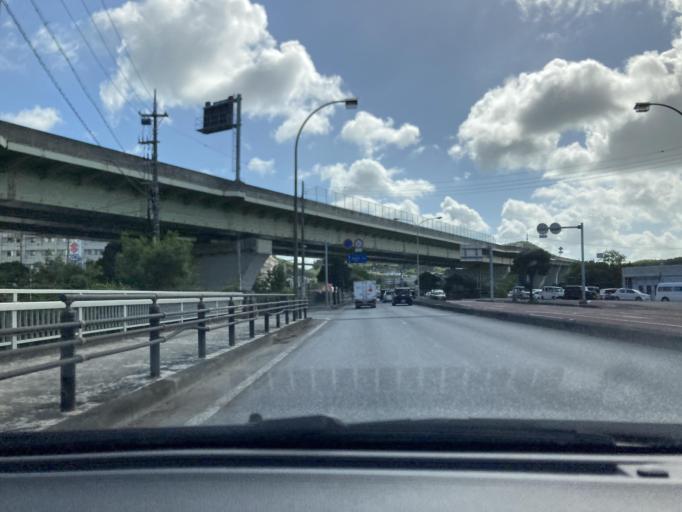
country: JP
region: Okinawa
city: Tomigusuku
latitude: 26.1803
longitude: 127.7163
